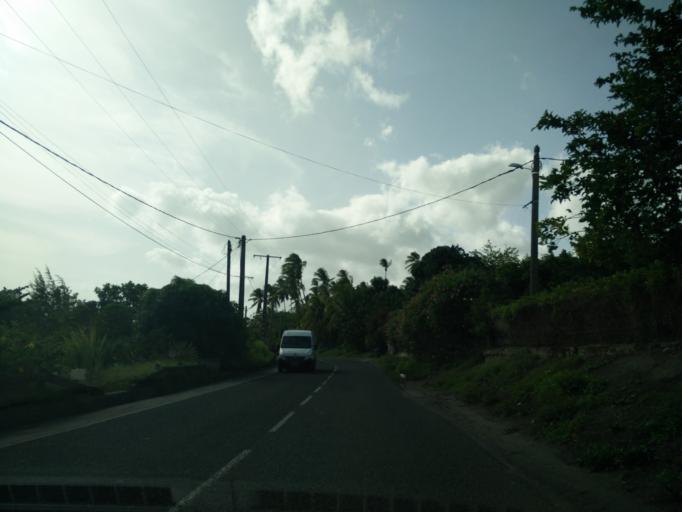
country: MQ
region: Martinique
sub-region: Martinique
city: Saint-Pierre
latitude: 14.7573
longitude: -61.1845
